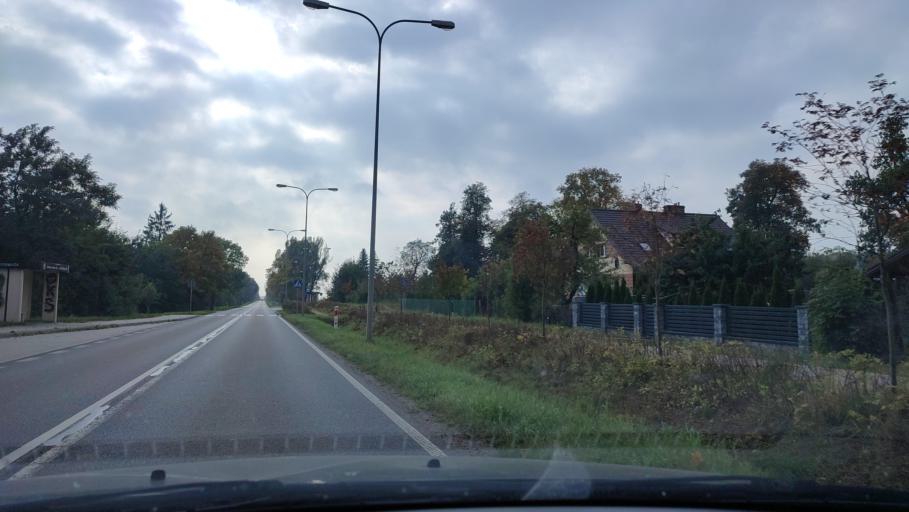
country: PL
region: Warmian-Masurian Voivodeship
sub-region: Powiat nidzicki
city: Nidzica
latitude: 53.3507
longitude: 20.3581
